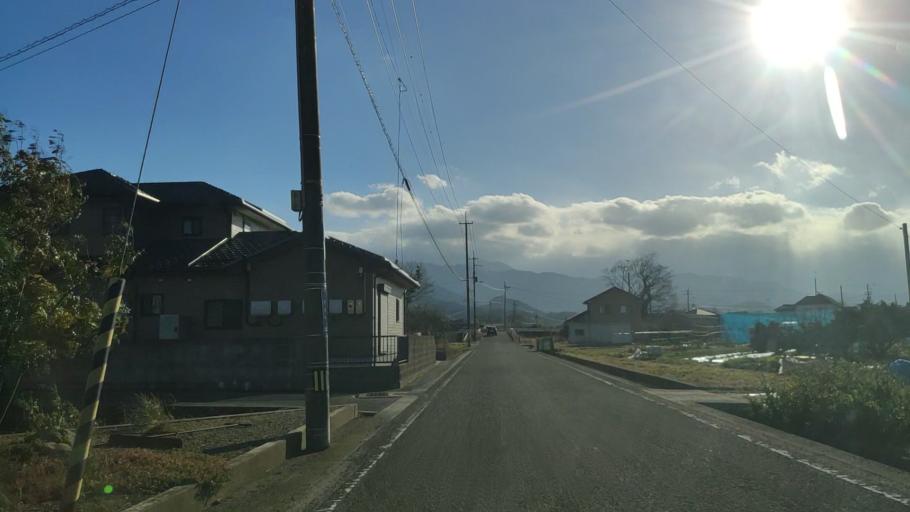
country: JP
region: Ehime
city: Saijo
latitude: 33.9098
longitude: 133.0972
